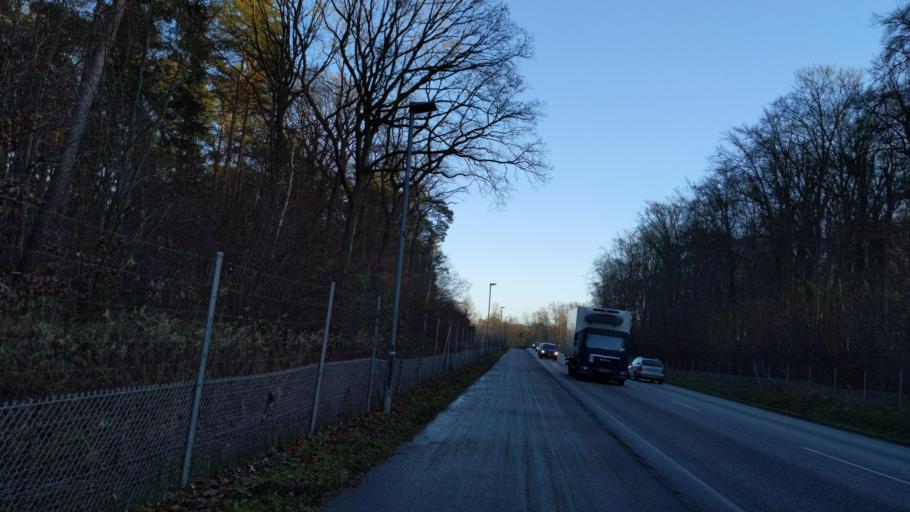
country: DE
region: Schleswig-Holstein
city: Ratekau
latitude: 53.8911
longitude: 10.7649
